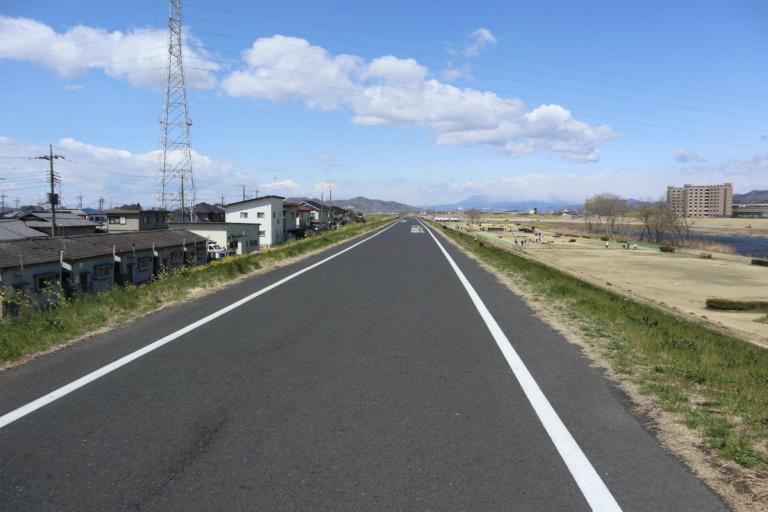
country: JP
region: Tochigi
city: Ashikaga
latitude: 36.3334
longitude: 139.4254
